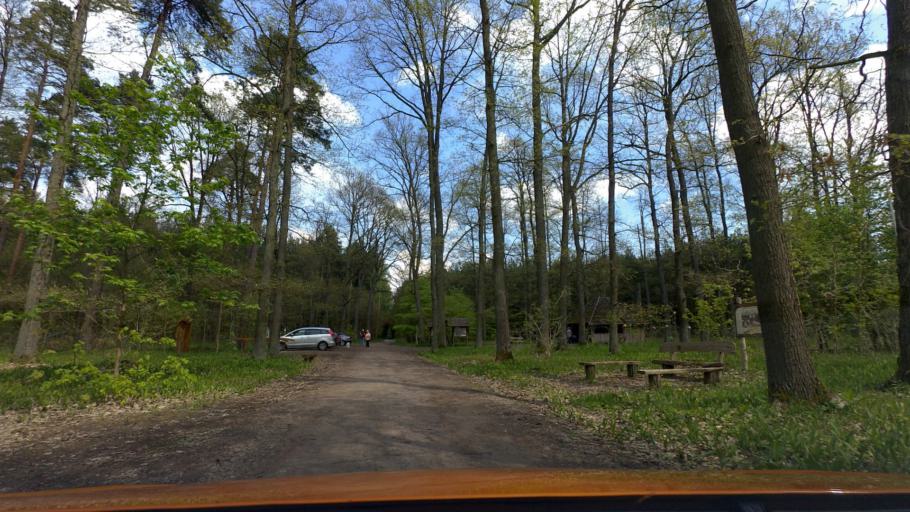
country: DE
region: Brandenburg
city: Spreenhagen
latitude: 52.3950
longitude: 13.9497
